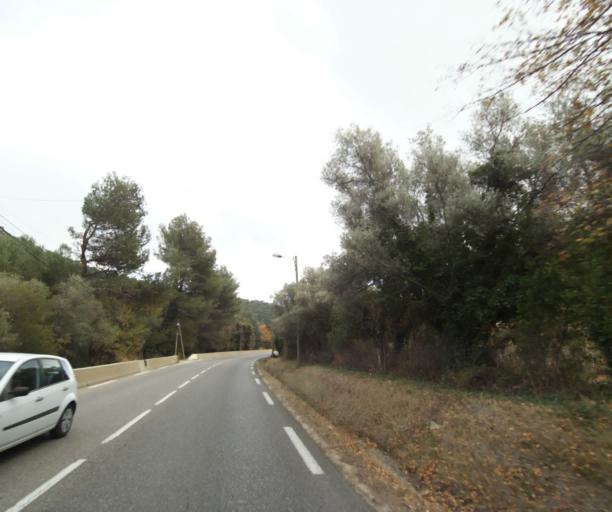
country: FR
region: Provence-Alpes-Cote d'Azur
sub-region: Departement des Bouches-du-Rhone
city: Gemenos
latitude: 43.2719
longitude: 5.6437
